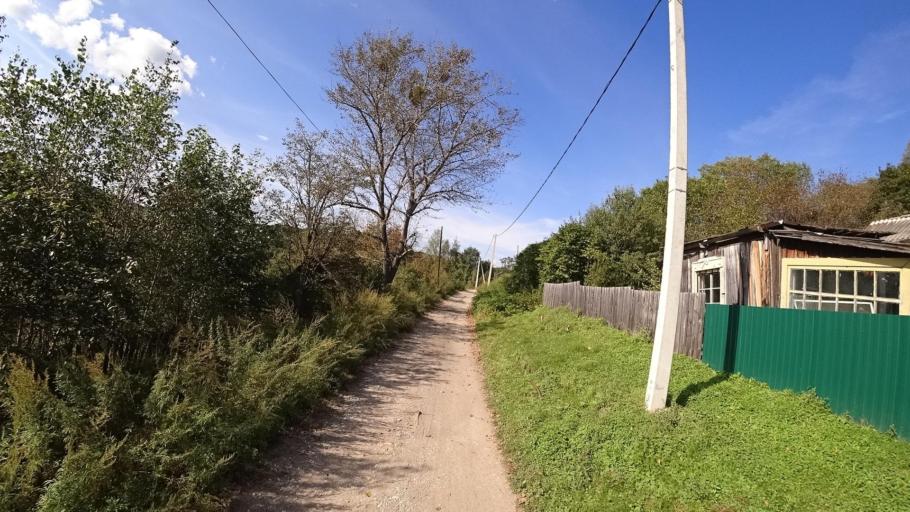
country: RU
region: Jewish Autonomous Oblast
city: Birakan
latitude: 49.0011
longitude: 131.7212
